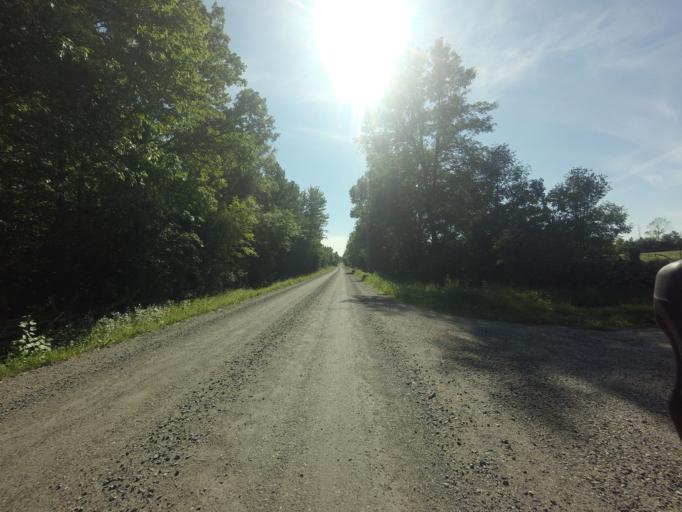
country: CA
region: Ontario
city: Perth
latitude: 44.9471
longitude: -76.3603
